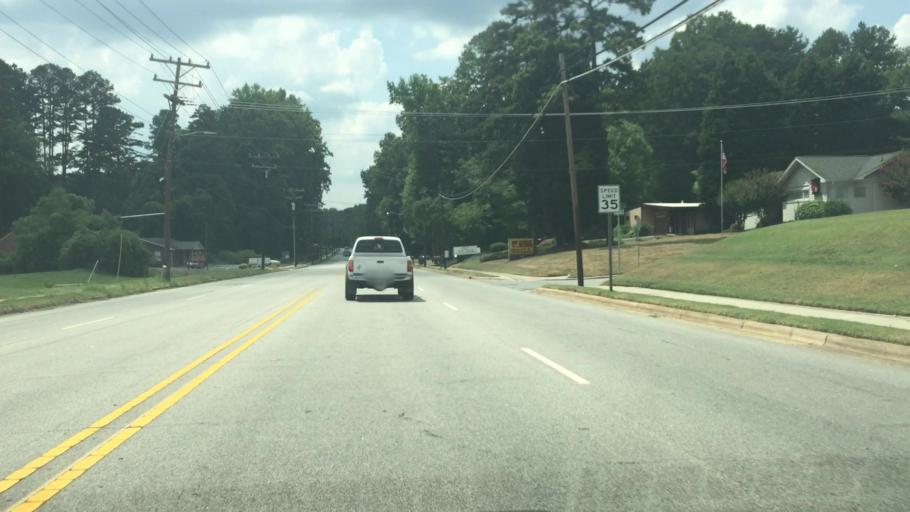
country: US
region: North Carolina
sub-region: Rowan County
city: Salisbury
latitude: 35.6877
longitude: -80.4874
